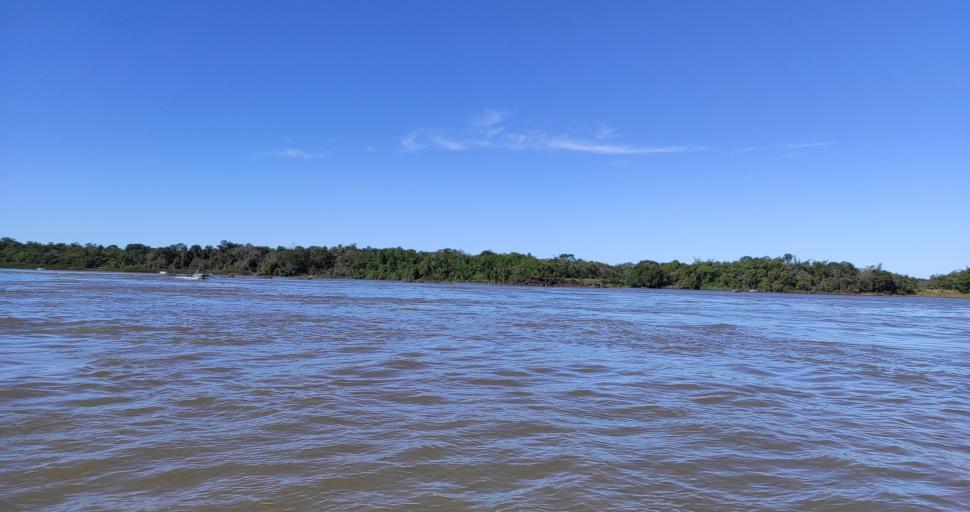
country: AR
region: Corrientes
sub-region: Departamento de Itati
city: Itati
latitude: -27.2766
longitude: -58.3226
